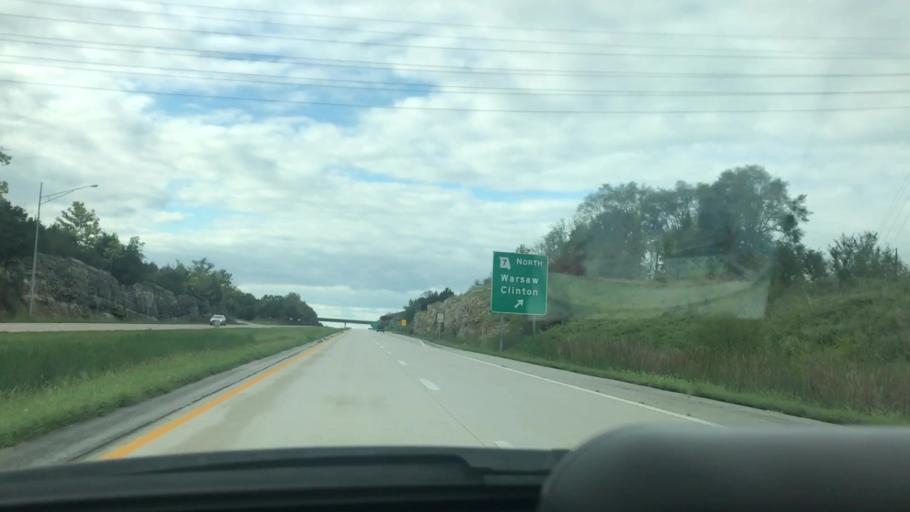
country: US
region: Missouri
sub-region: Benton County
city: Warsaw
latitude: 38.2482
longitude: -93.3612
